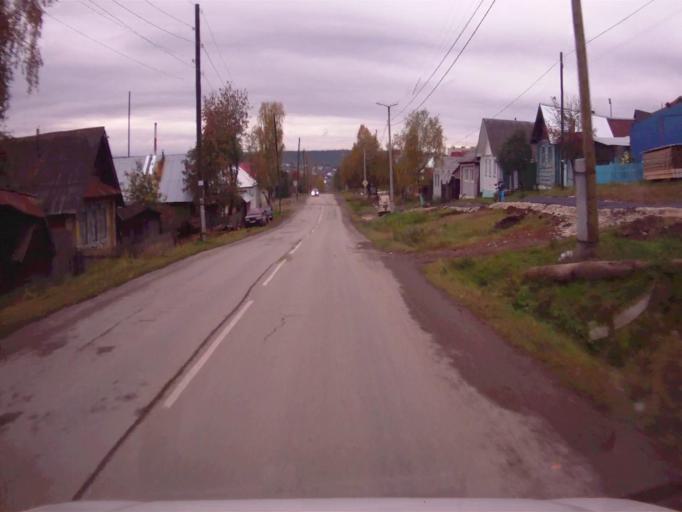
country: RU
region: Chelyabinsk
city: Nyazepetrovsk
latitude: 56.0584
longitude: 59.6093
